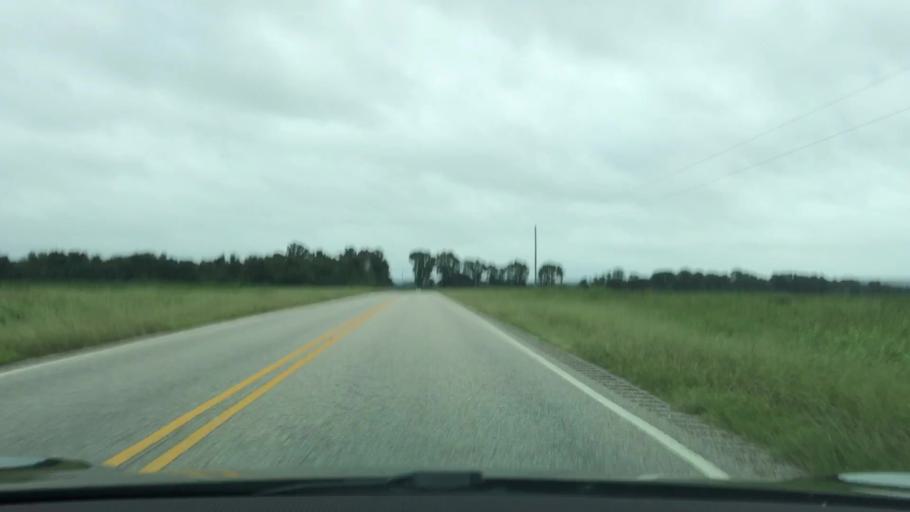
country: US
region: Alabama
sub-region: Covington County
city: Opp
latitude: 31.2883
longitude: -86.1474
